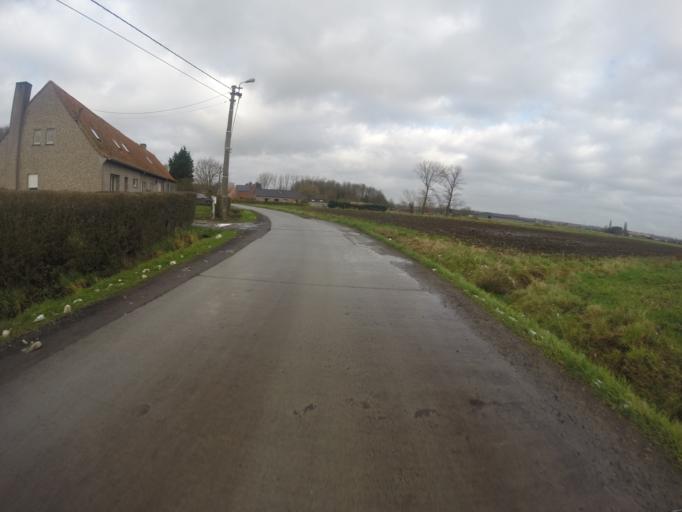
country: BE
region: Flanders
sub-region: Provincie Oost-Vlaanderen
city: Zomergem
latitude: 51.1392
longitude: 3.5238
